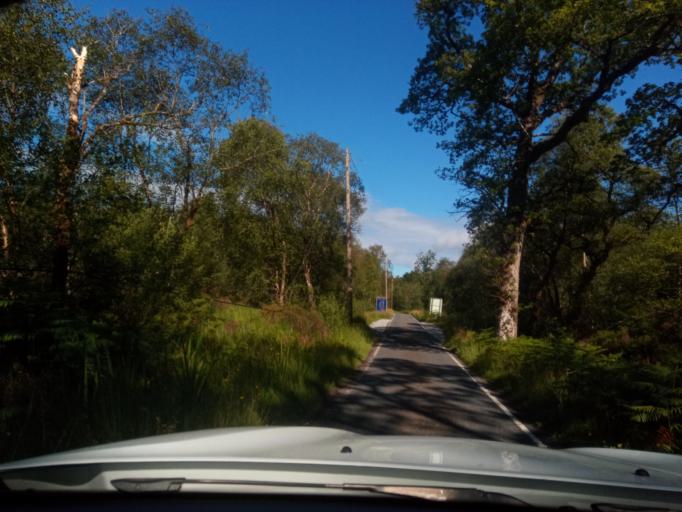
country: GB
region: Scotland
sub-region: Argyll and Bute
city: Isle Of Mull
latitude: 56.6945
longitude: -5.6825
